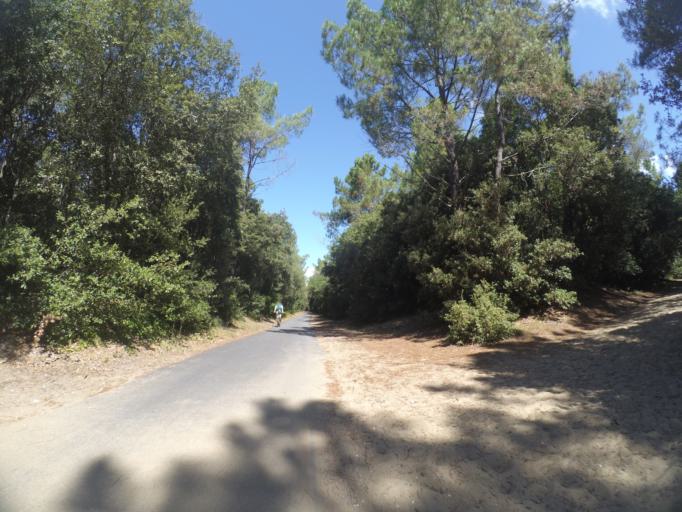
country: FR
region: Poitou-Charentes
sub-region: Departement de la Charente-Maritime
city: Les Mathes
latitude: 45.6745
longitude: -1.1507
